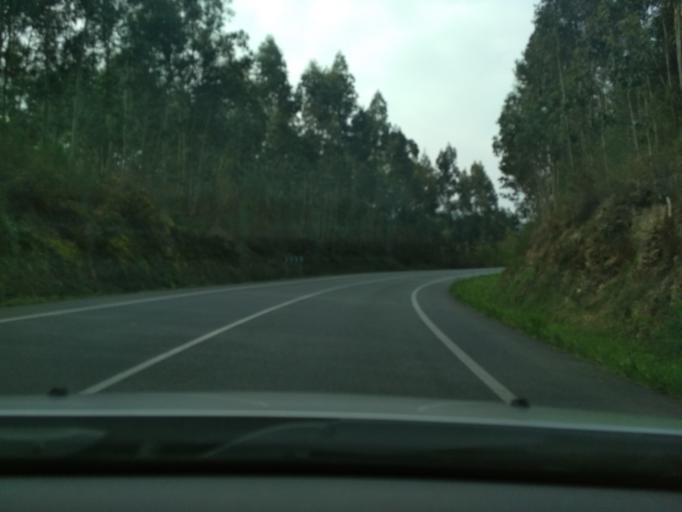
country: ES
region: Galicia
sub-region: Provincia de Pontevedra
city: Catoira
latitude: 42.6612
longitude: -8.7022
